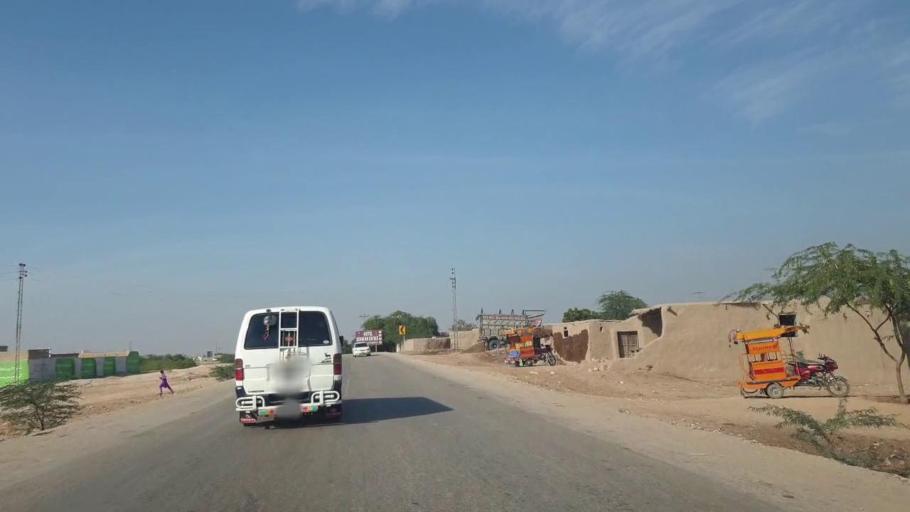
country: PK
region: Sindh
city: Sehwan
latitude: 26.3853
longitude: 67.8709
